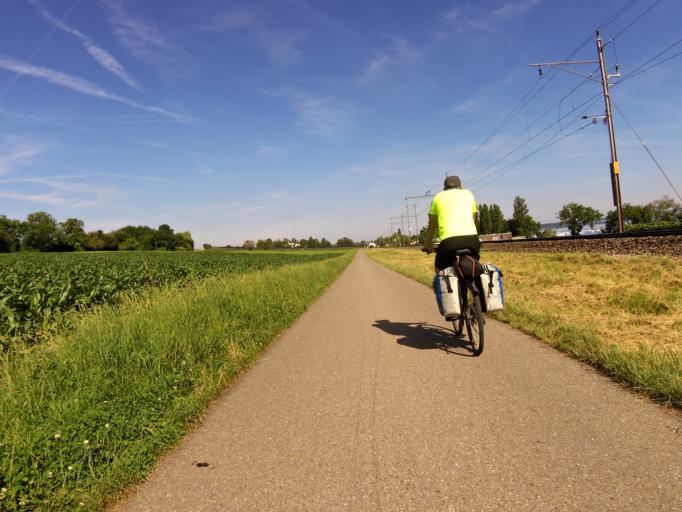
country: CH
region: Thurgau
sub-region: Kreuzlingen District
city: Altnau
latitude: 47.6240
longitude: 9.2598
